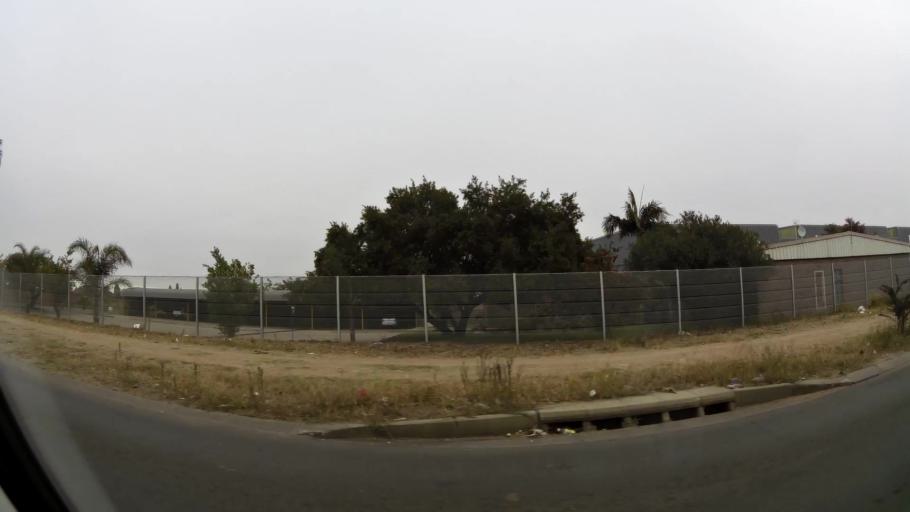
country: ZA
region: Limpopo
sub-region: Capricorn District Municipality
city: Polokwane
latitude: -23.8450
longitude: 29.3991
